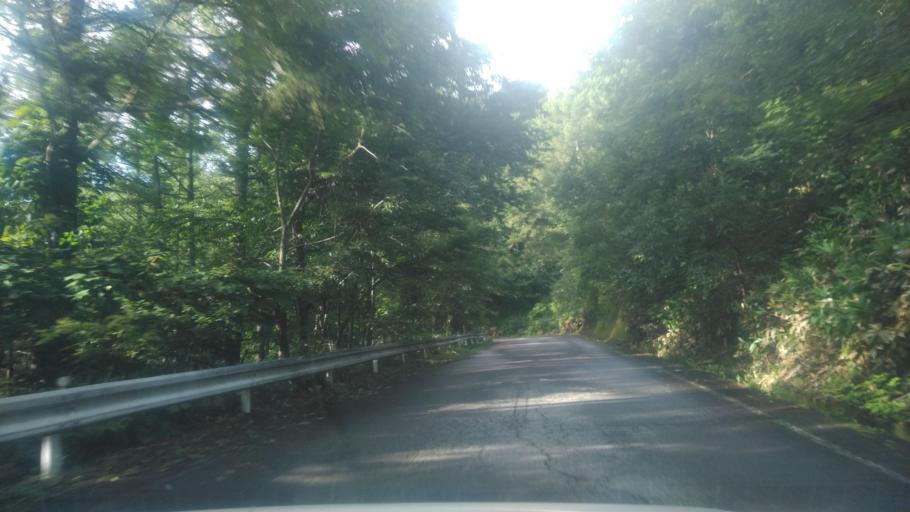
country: JP
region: Nagano
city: Ueda
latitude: 36.5054
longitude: 138.3750
